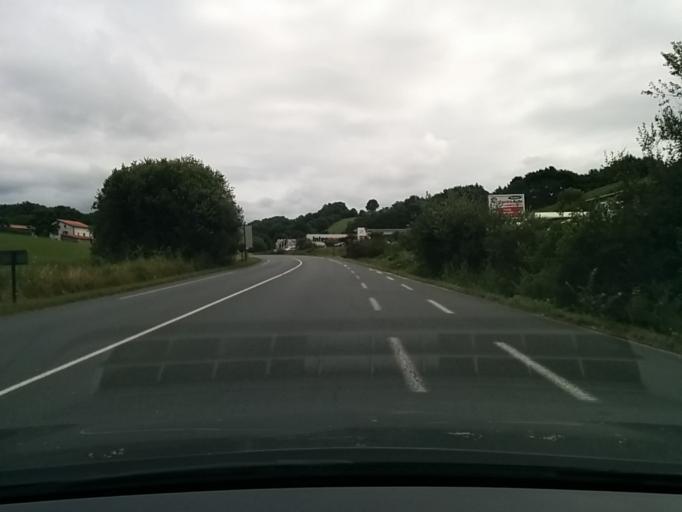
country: FR
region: Aquitaine
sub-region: Departement des Pyrenees-Atlantiques
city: Cambo-les-Bains
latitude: 43.3513
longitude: -1.4161
